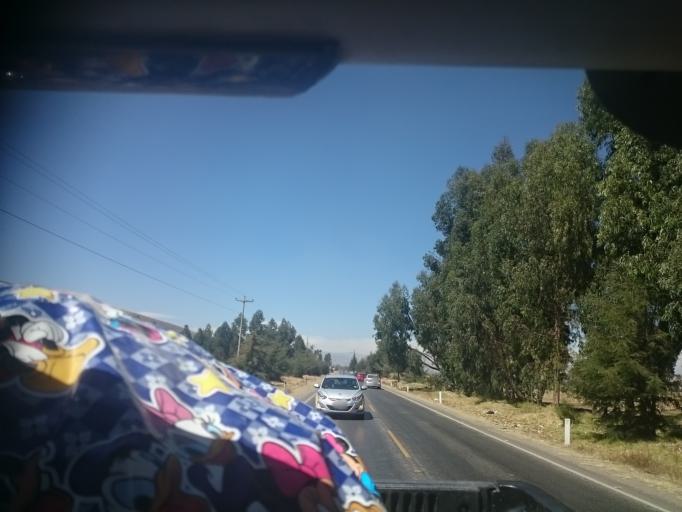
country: PE
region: Junin
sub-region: Provincia de Jauja
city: Huamali
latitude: -11.8200
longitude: -75.4156
